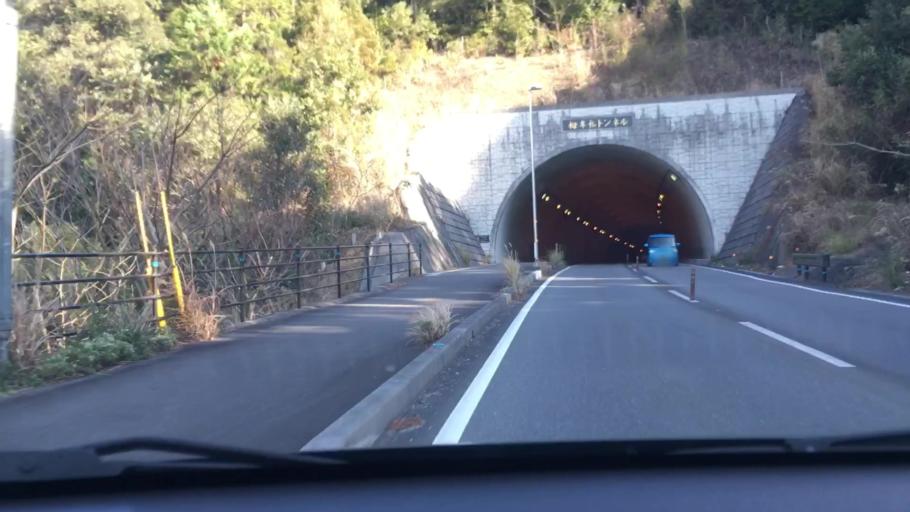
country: JP
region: Oita
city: Saiki
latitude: 32.9606
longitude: 131.8488
